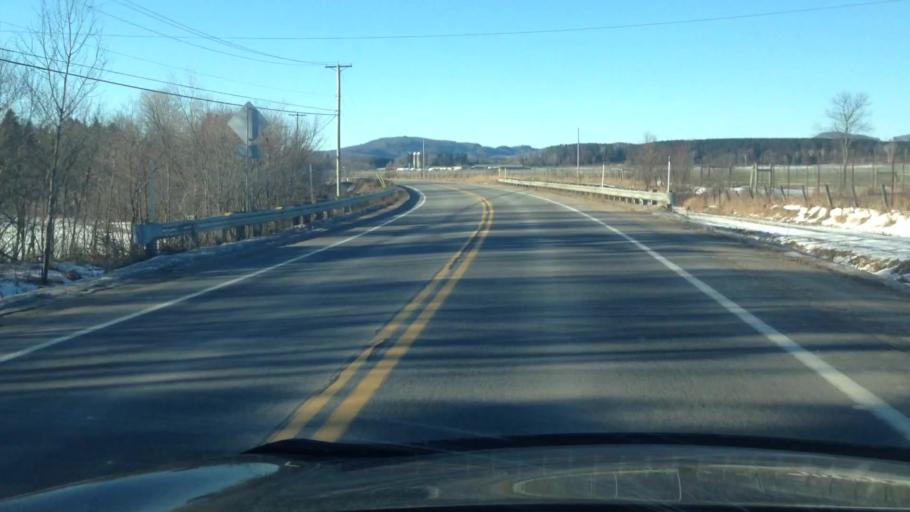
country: CA
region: Quebec
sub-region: Laurentides
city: Mont-Tremblant
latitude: 45.9621
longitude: -74.5841
